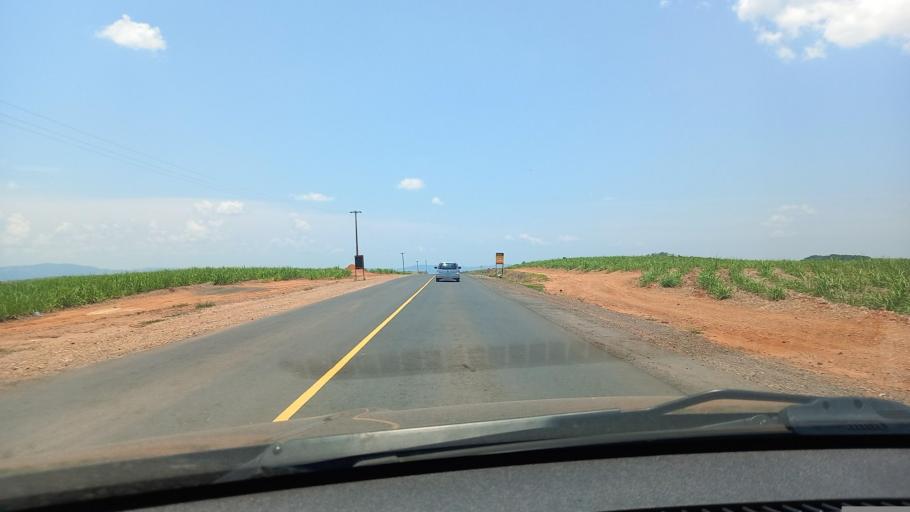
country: BR
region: Sao Paulo
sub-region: Itapira
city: Itapira
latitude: -22.3894
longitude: -46.8640
